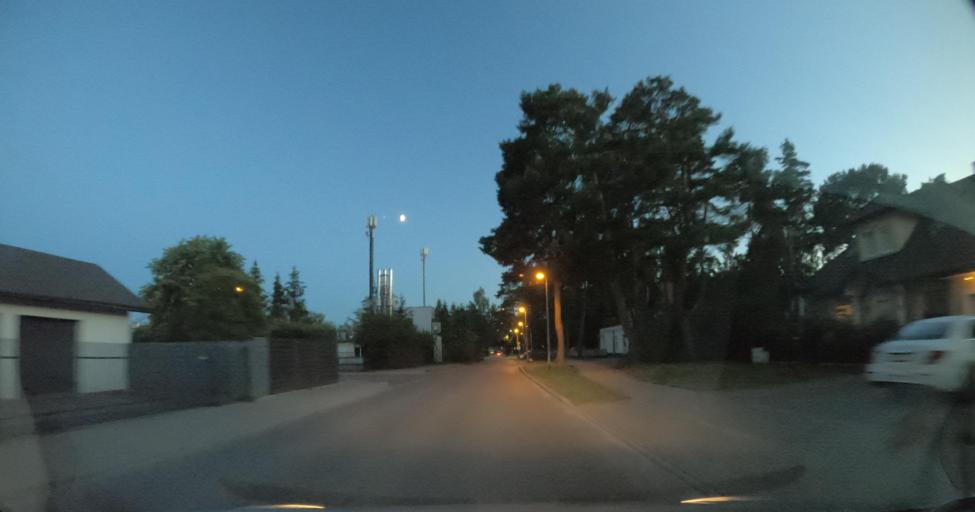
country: PL
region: Pomeranian Voivodeship
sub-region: Gdynia
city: Wielki Kack
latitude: 54.4293
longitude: 18.4690
